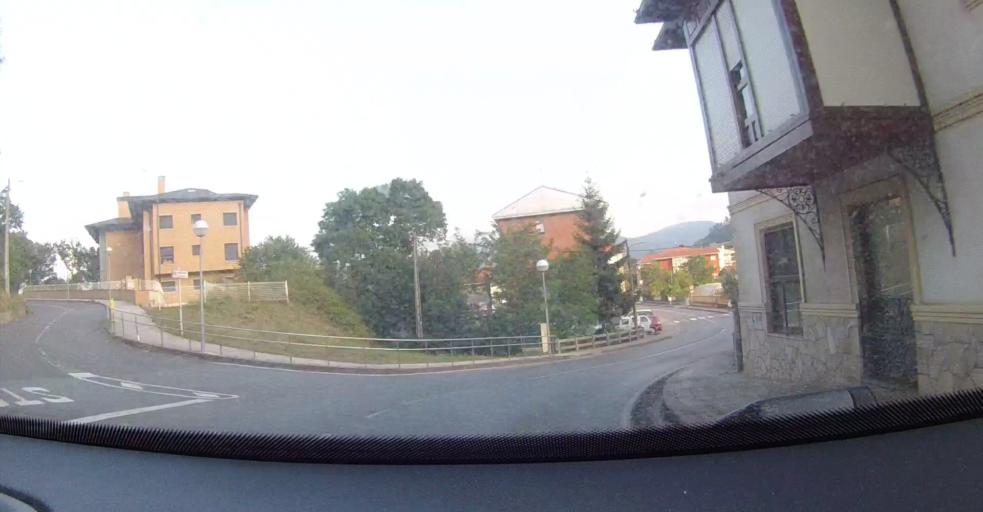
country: ES
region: Basque Country
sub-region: Bizkaia
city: Sopuerta
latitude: 43.2766
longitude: -3.1581
